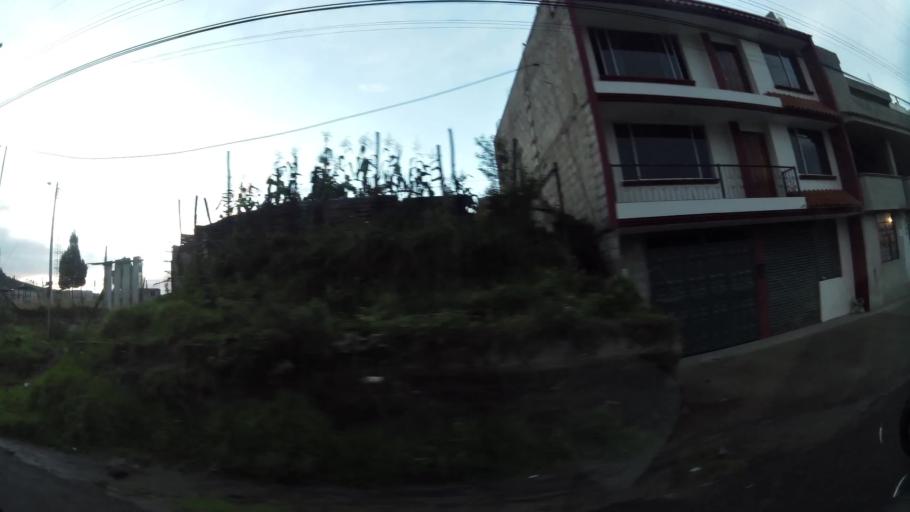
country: EC
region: Pichincha
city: Quito
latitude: -0.0960
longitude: -78.5267
